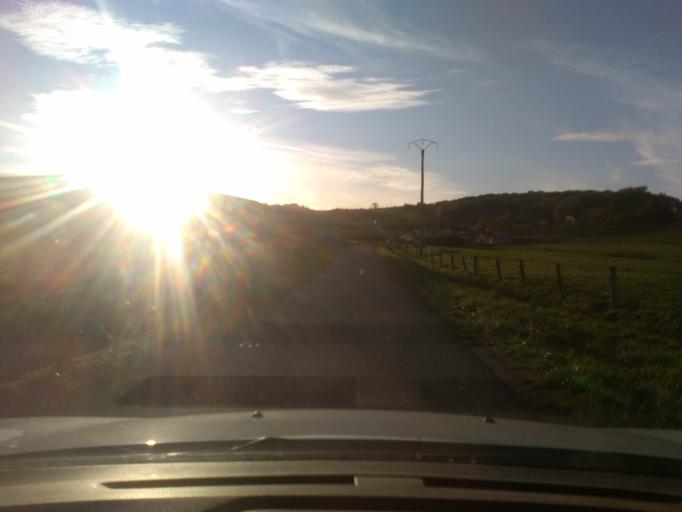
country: FR
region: Lorraine
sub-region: Departement des Vosges
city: Charmes
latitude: 48.3357
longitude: 6.2805
